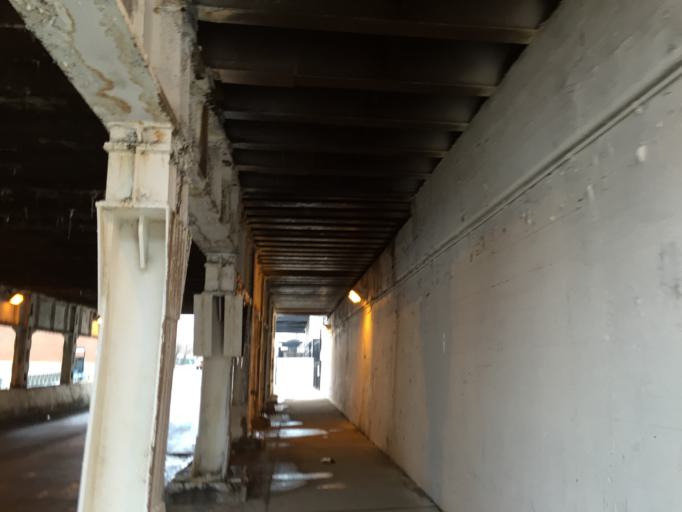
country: US
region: Illinois
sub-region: Cook County
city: Chicago
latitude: 41.8608
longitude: -87.6565
